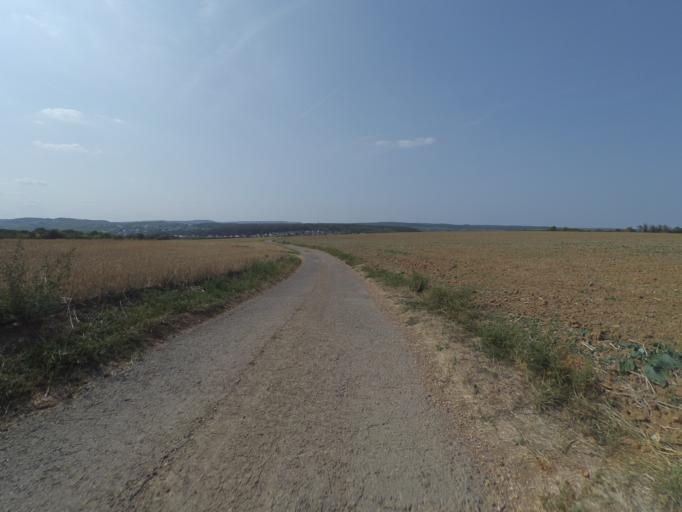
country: LU
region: Grevenmacher
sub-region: Canton de Remich
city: Remich
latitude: 49.5502
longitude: 6.3950
